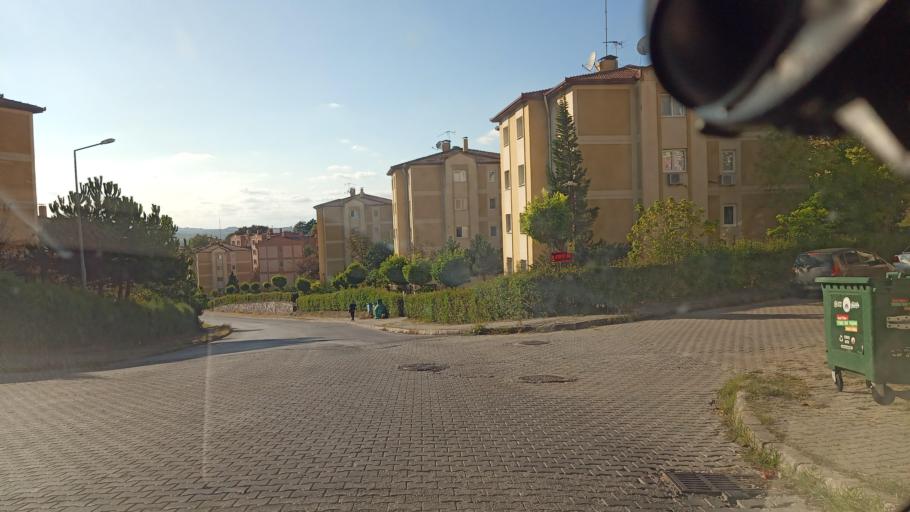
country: TR
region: Kocaeli
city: Kaymaz
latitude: 40.8613
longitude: 30.2899
